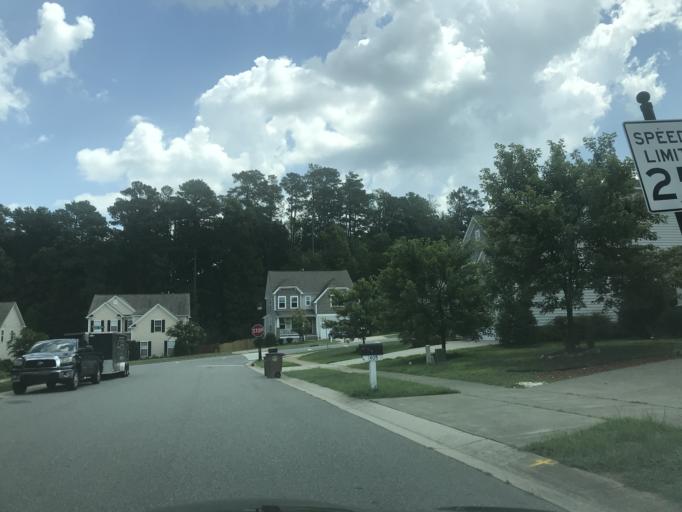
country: US
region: North Carolina
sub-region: Wake County
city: Wake Forest
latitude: 35.9616
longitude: -78.5291
